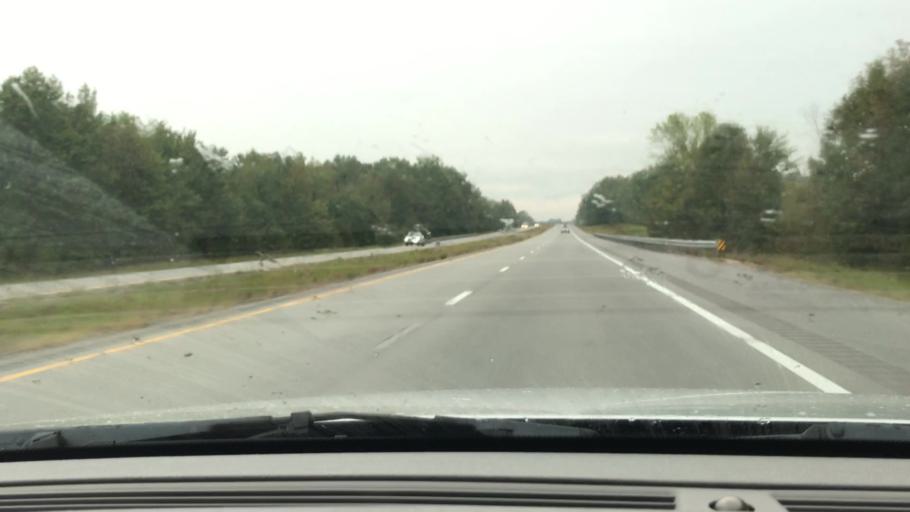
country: US
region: Kentucky
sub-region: Barren County
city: Glasgow
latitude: 37.0253
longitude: -86.0429
